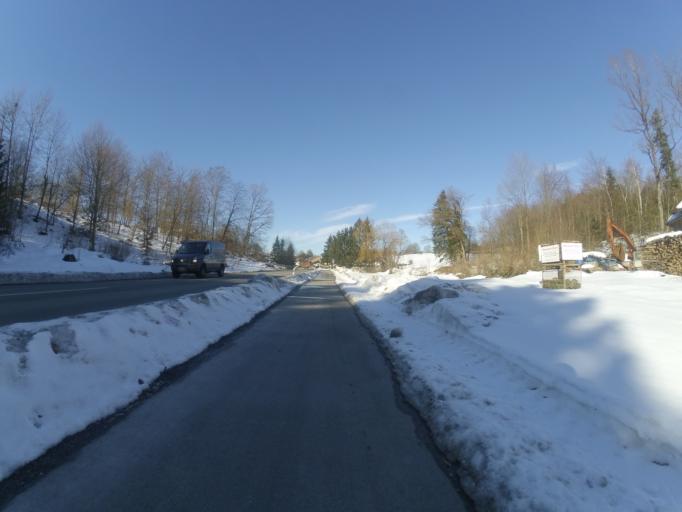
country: DE
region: Bavaria
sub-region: Upper Bavaria
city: Aying
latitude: 47.9586
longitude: 11.7839
